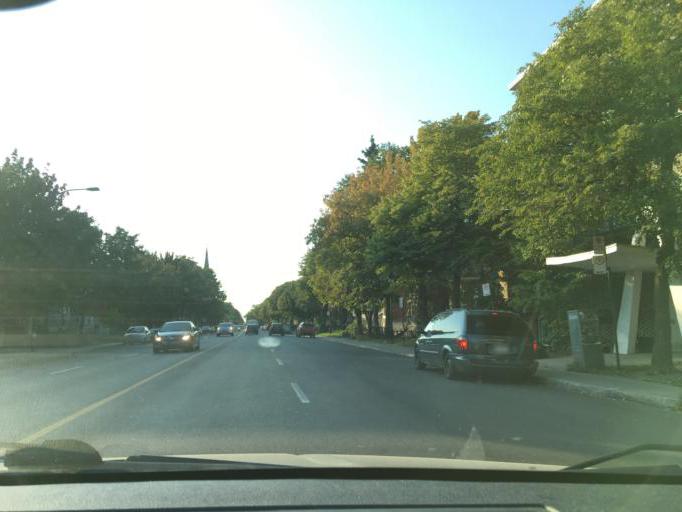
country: CA
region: Quebec
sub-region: Montreal
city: Montreal
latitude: 45.5465
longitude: -73.6037
